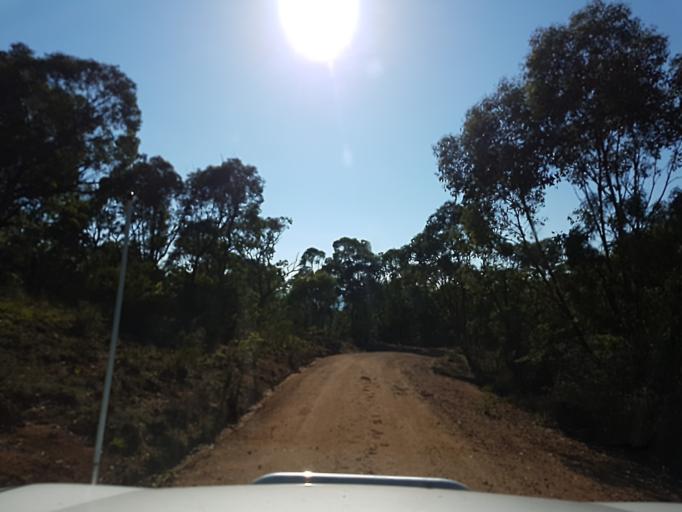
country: AU
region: New South Wales
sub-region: Snowy River
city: Jindabyne
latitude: -36.9336
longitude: 148.3395
